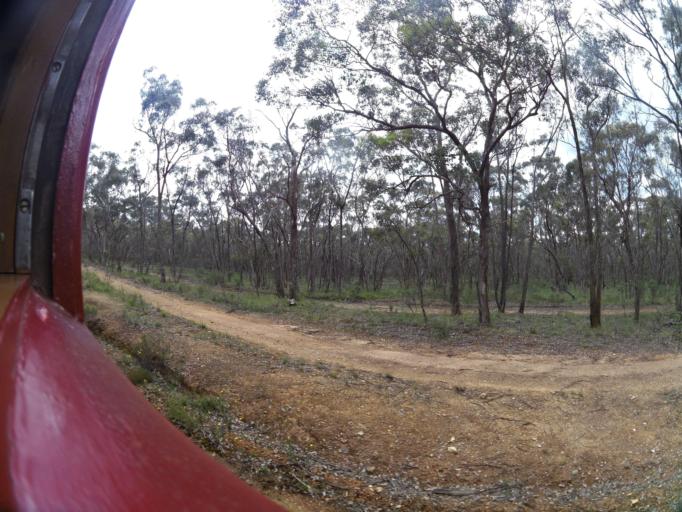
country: AU
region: Victoria
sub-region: Mount Alexander
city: Castlemaine
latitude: -37.0063
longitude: 144.1203
